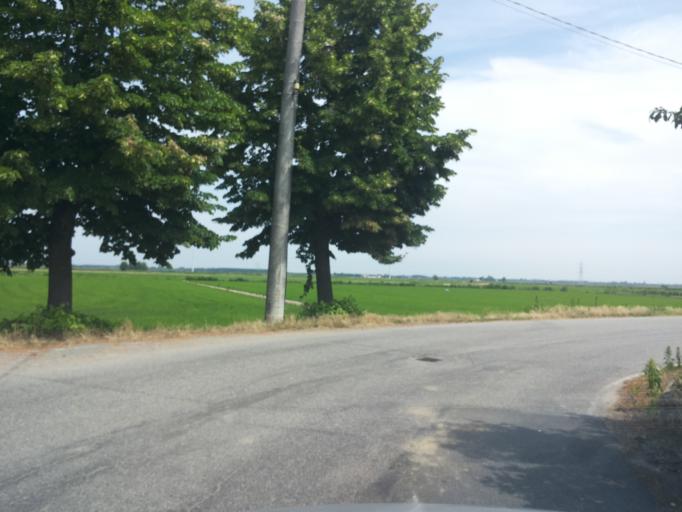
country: IT
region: Piedmont
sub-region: Provincia di Vercelli
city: Pezzana
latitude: 45.2644
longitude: 8.4921
